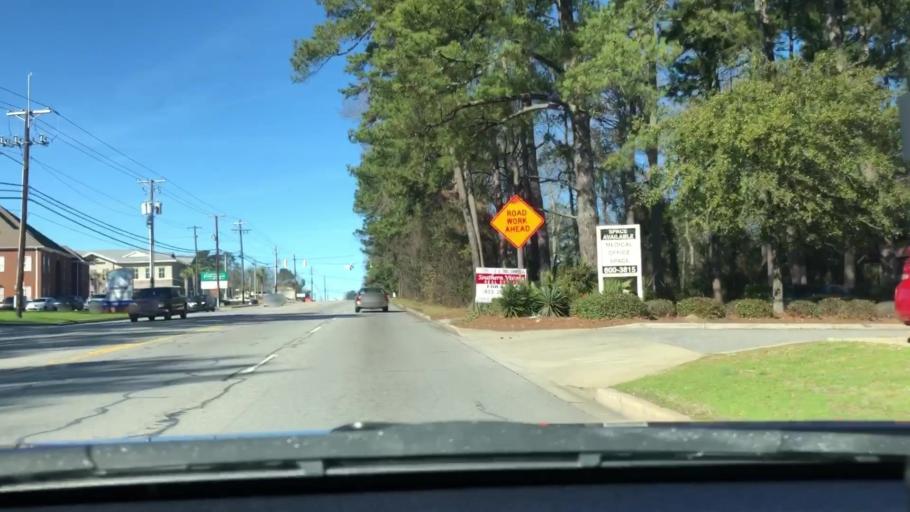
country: US
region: South Carolina
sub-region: Lexington County
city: Oak Grove
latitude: 34.0065
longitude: -81.1219
